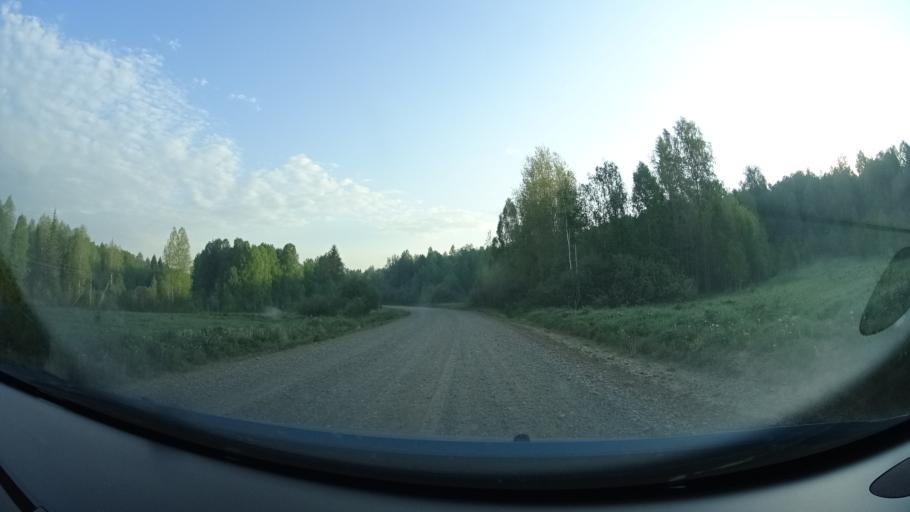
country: RU
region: Perm
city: Barda
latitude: 56.7090
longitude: 55.6767
